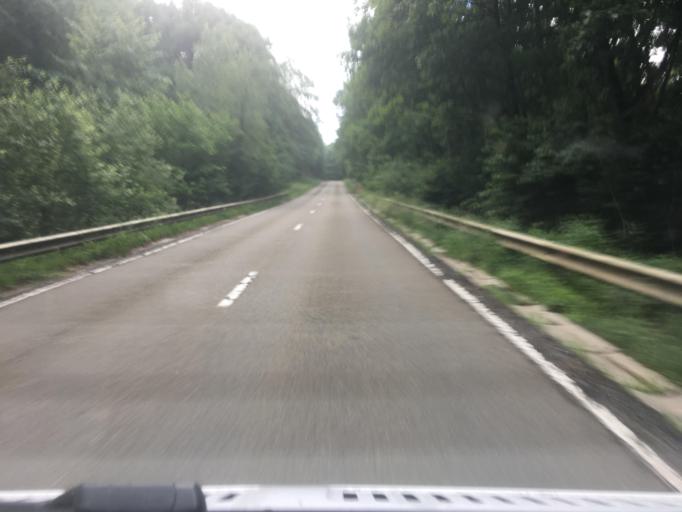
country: BE
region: Wallonia
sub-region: Province du Luxembourg
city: Florenville
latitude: 49.6702
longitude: 5.3349
